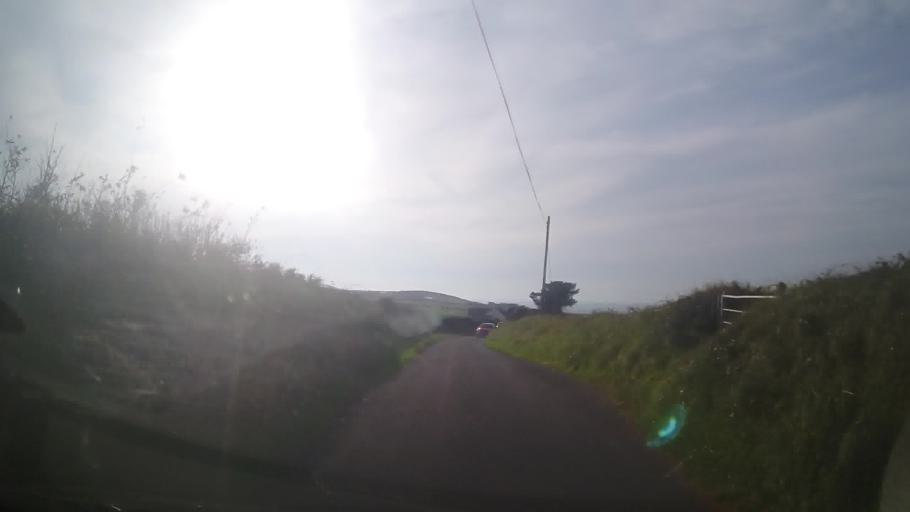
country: GB
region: Wales
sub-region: Pembrokeshire
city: Llanrhian
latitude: 51.9292
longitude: -5.1906
